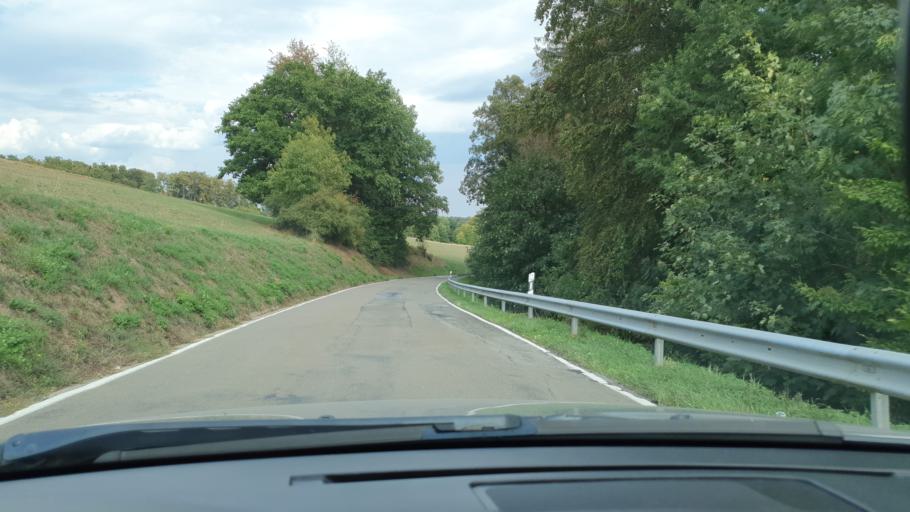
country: DE
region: Rheinland-Pfalz
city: Kashofen
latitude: 49.3342
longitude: 7.4304
